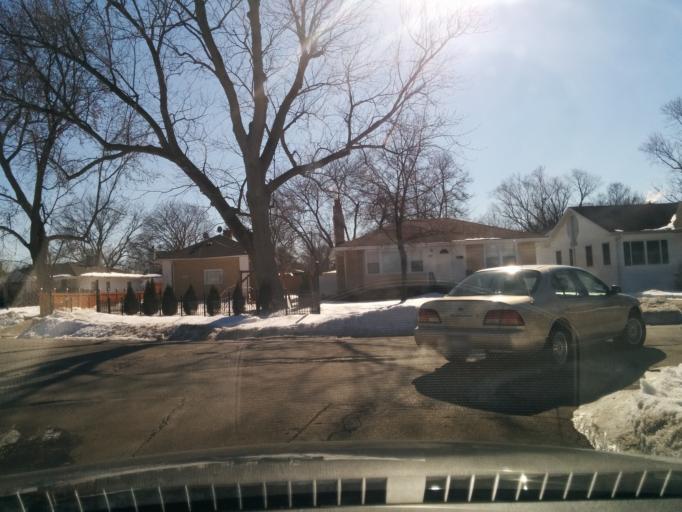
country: US
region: Illinois
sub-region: DuPage County
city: Villa Park
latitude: 41.8946
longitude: -87.9737
